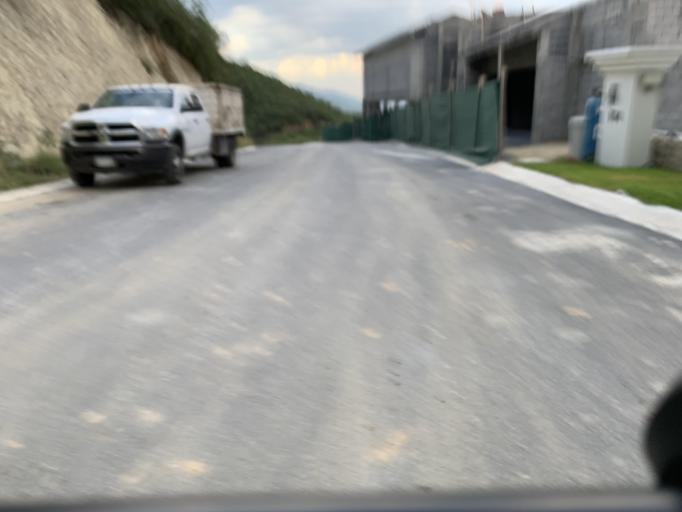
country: MX
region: Nuevo Leon
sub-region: Juarez
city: Bosques de San Pedro
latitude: 25.5133
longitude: -100.1816
